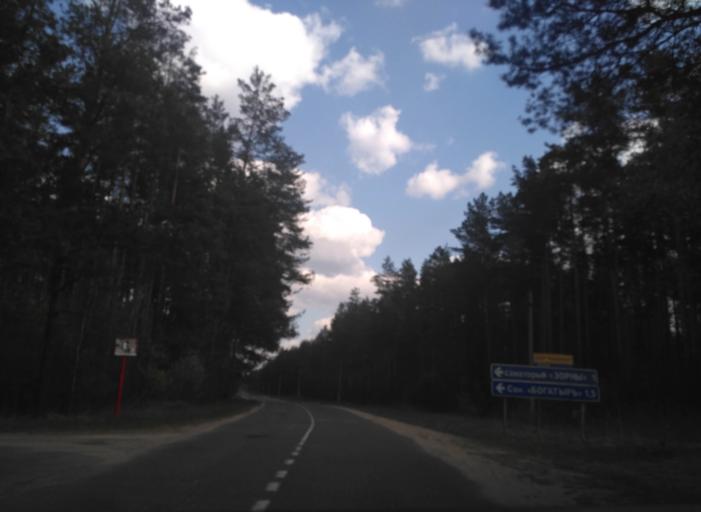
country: BY
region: Minsk
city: Radashkovichy
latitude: 54.1851
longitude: 27.2569
